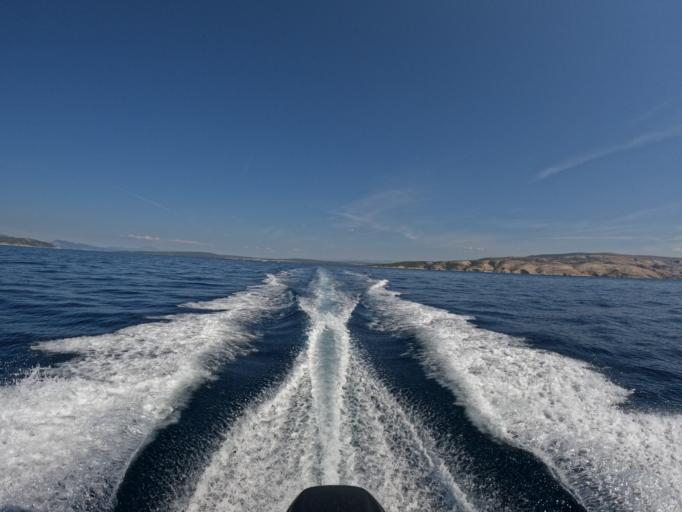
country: HR
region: Primorsko-Goranska
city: Punat
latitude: 44.9419
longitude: 14.6156
